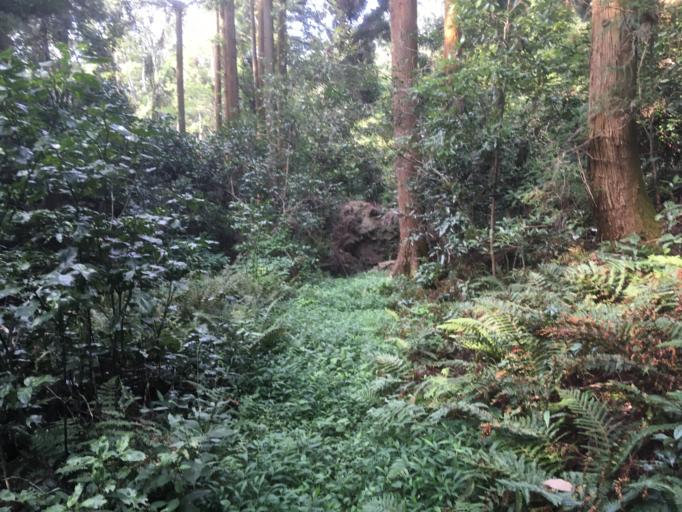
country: JP
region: Nara
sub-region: Ikoma-shi
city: Ikoma
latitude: 34.6976
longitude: 135.6641
